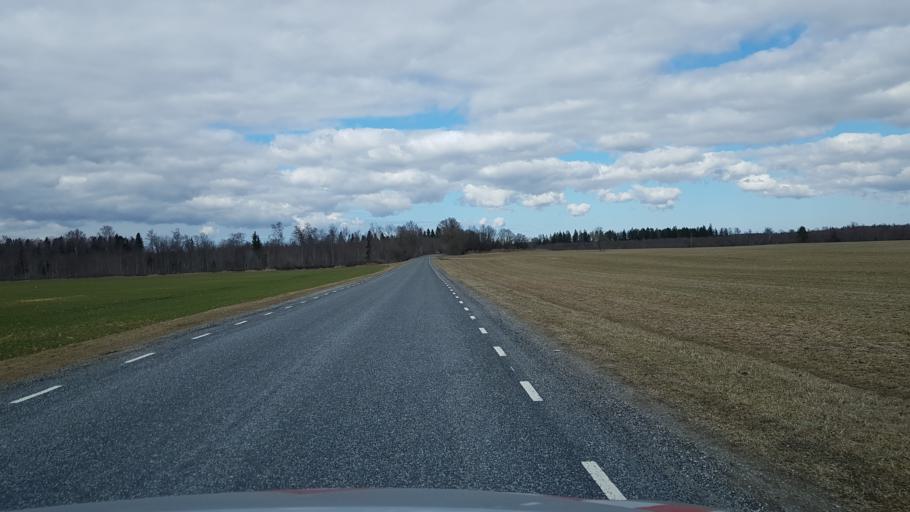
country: EE
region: Laeaene-Virumaa
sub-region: Tamsalu vald
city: Tamsalu
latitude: 59.1804
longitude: 26.1276
